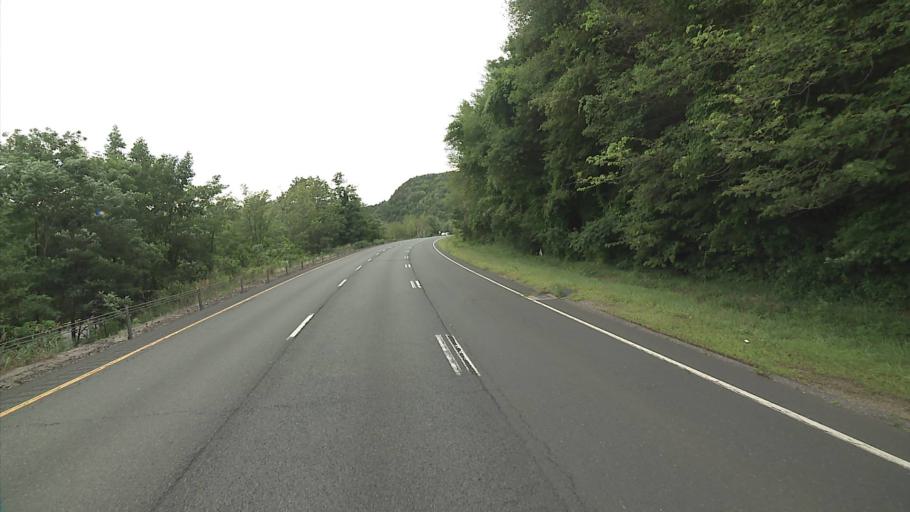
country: US
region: Connecticut
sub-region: Litchfield County
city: Thomaston
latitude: 41.6357
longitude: -73.0793
